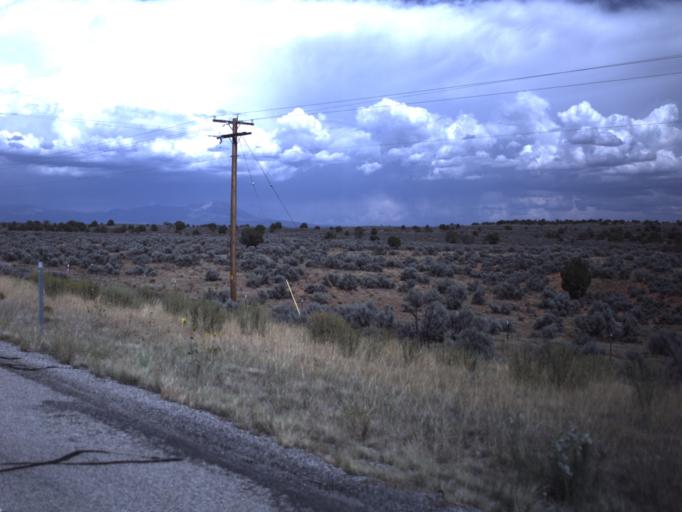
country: US
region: Utah
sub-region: San Juan County
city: Blanding
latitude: 37.4913
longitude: -109.4796
